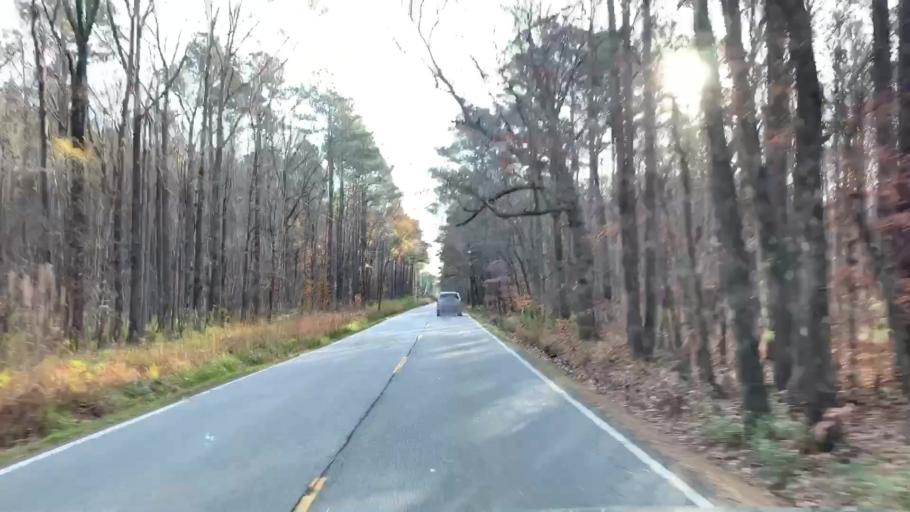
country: US
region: Virginia
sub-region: City of Virginia Beach
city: Virginia Beach
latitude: 36.7398
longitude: -76.1093
